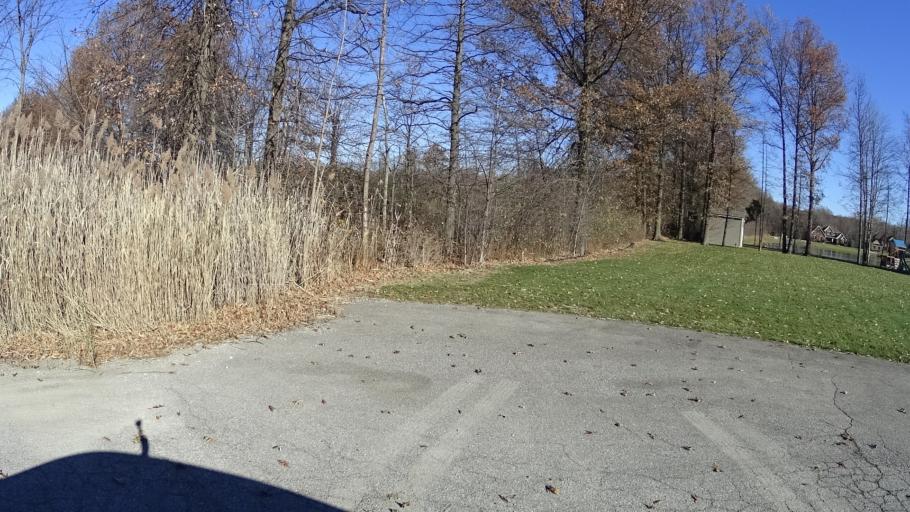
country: US
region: Ohio
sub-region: Lorain County
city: Avon Center
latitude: 41.4447
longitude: -81.9830
